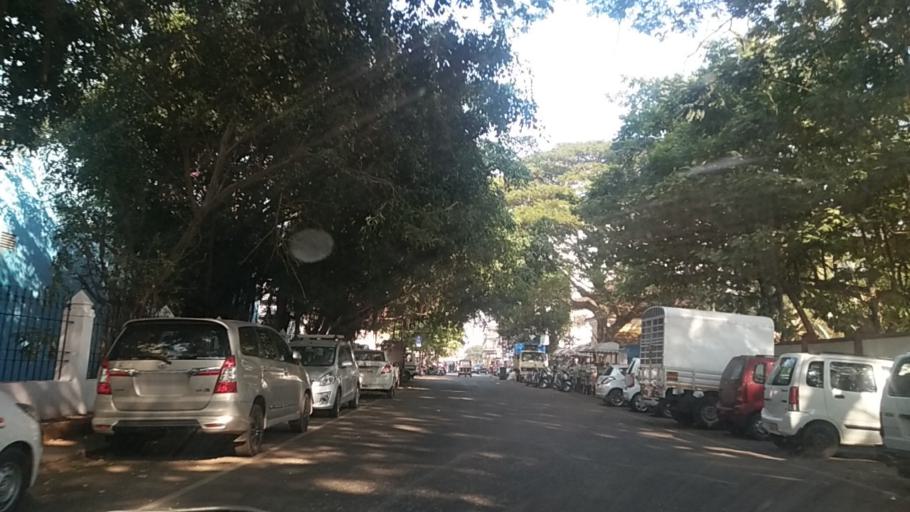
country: IN
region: Goa
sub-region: North Goa
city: Panaji
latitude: 15.4983
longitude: 73.8211
